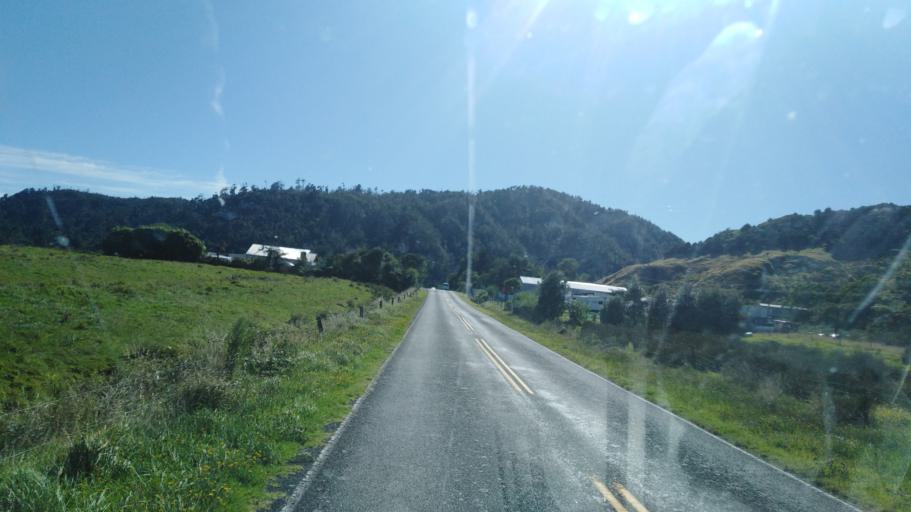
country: NZ
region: West Coast
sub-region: Buller District
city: Westport
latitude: -41.5326
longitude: 171.9383
